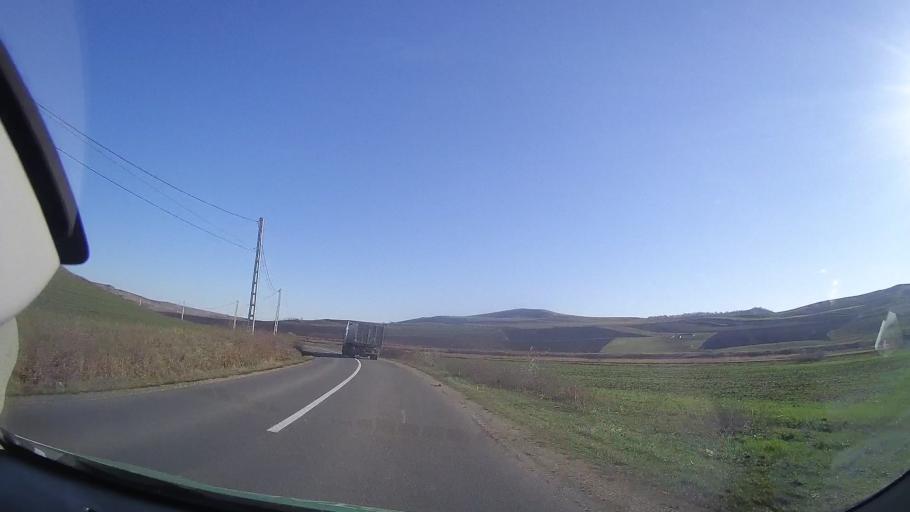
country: RO
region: Mures
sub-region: Comuna Mihesu de Campie
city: Mihesu de Campie
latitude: 46.6496
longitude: 24.1657
